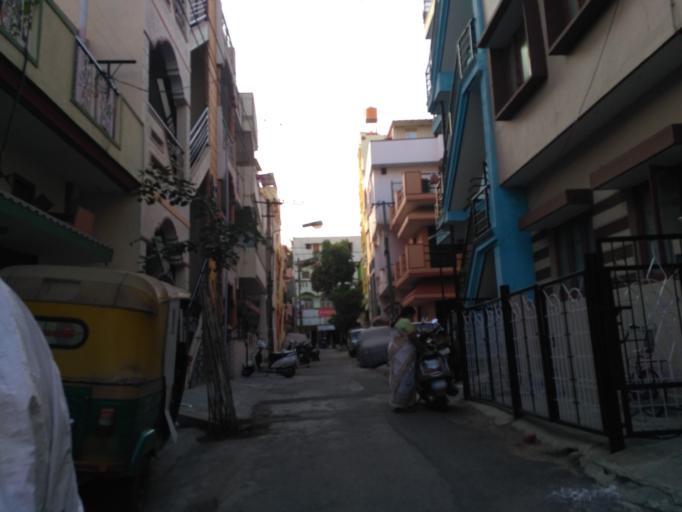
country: IN
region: Karnataka
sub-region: Bangalore Urban
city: Bangalore
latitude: 12.9575
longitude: 77.5333
